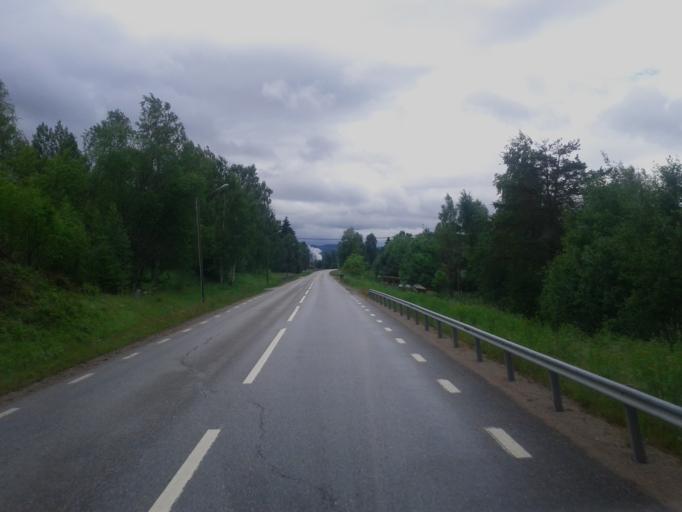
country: SE
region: Gaevleborg
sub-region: Nordanstigs Kommun
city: Bergsjoe
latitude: 62.0995
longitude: 16.7411
